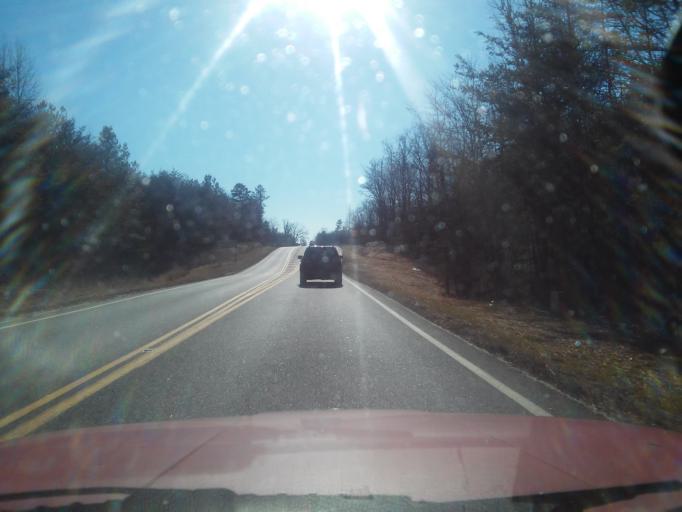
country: US
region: Virginia
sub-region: Fluvanna County
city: Palmyra
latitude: 37.9920
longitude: -78.2007
